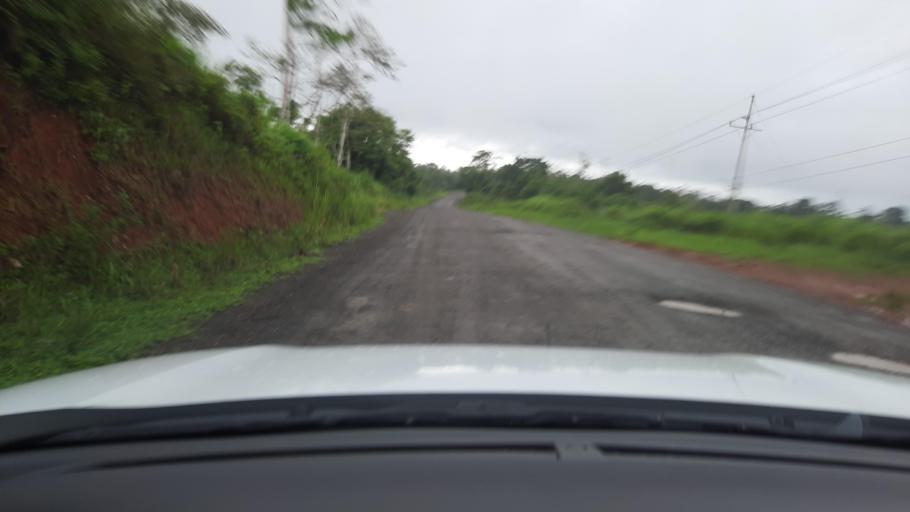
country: CR
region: Alajuela
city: San Jose
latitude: 11.0141
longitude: -85.3326
